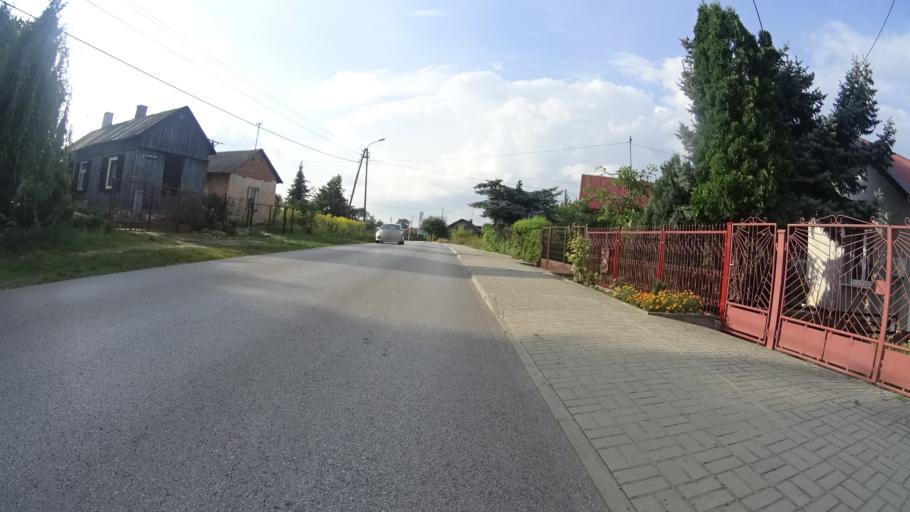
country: PL
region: Masovian Voivodeship
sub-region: Powiat grojecki
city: Mogielnica
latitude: 51.6863
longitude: 20.7298
